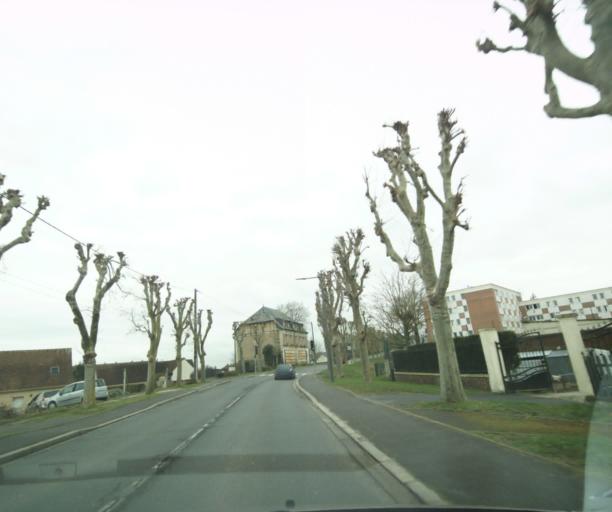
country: FR
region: Picardie
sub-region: Departement de l'Oise
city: Noyon
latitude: 49.5758
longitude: 3.0085
